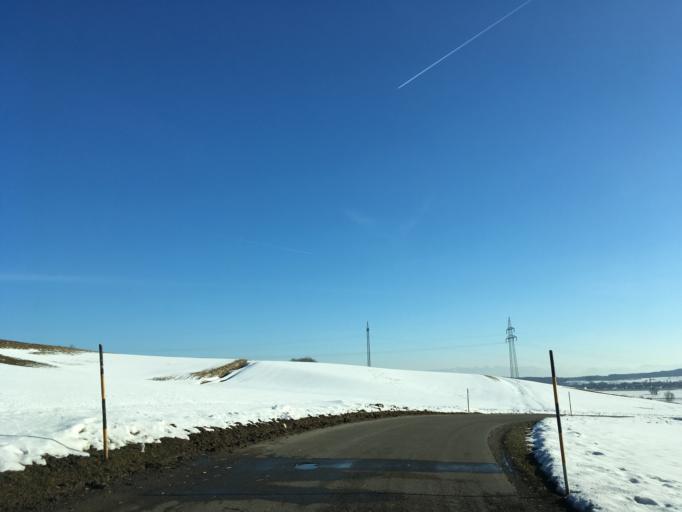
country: DE
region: Bavaria
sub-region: Upper Bavaria
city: Steinhoring
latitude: 48.1098
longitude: 12.0273
